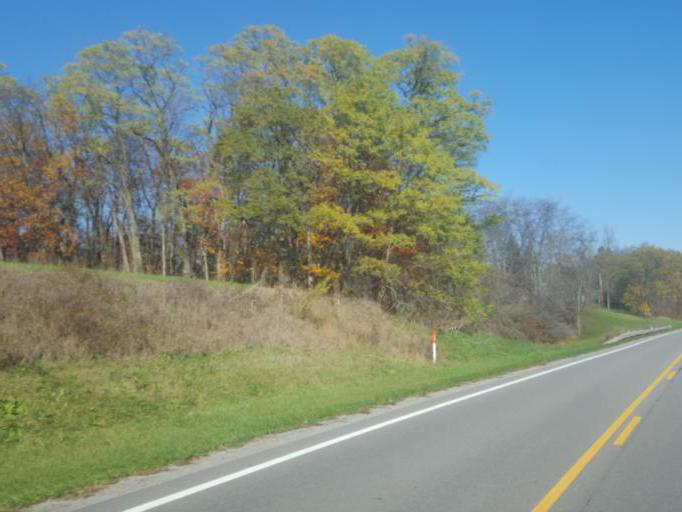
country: US
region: Ohio
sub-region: Wyandot County
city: Carey
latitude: 40.9678
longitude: -83.2740
